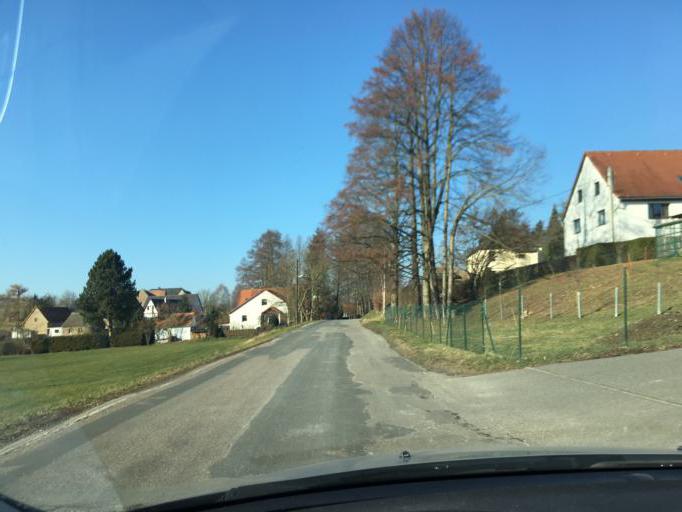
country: DE
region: Saxony
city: Penig
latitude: 50.9687
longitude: 12.7161
